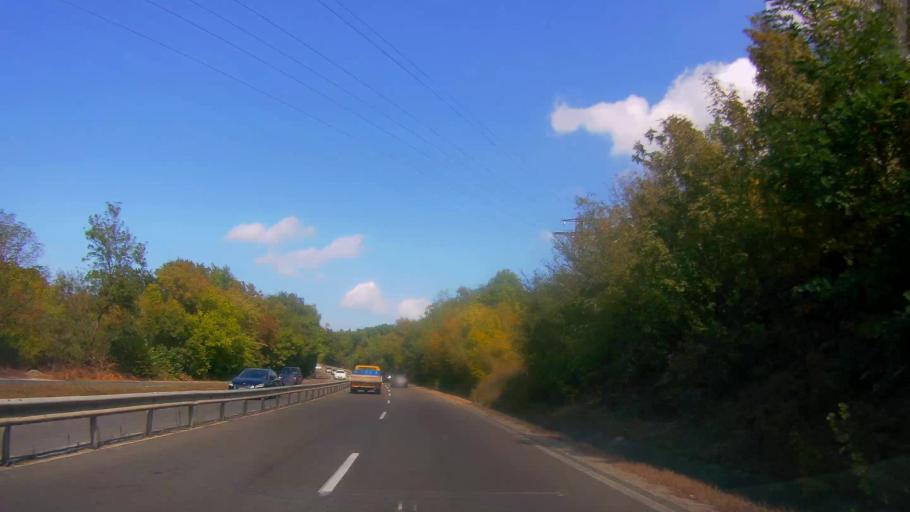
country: BG
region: Burgas
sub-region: Obshtina Burgas
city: Burgas
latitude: 42.4278
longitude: 27.5203
